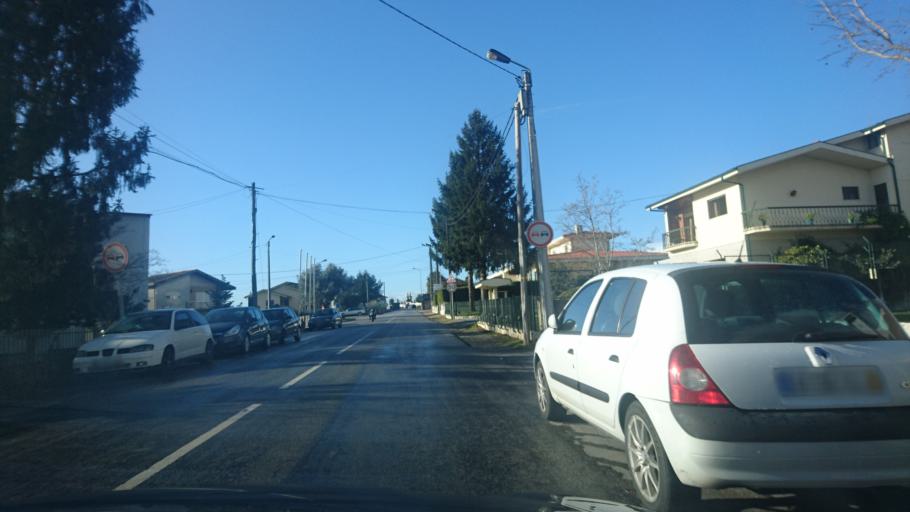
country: PT
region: Porto
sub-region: Paredes
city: Recarei
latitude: 41.1454
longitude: -8.3892
